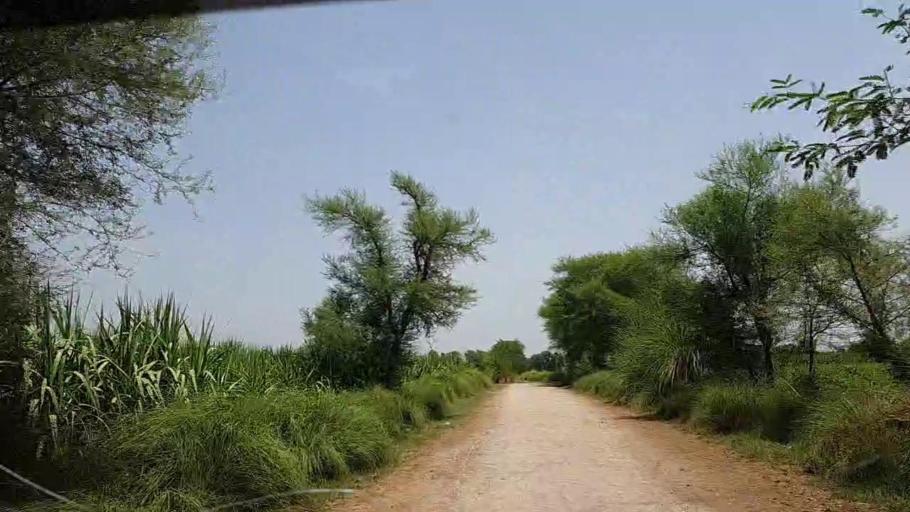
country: PK
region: Sindh
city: Tharu Shah
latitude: 26.9354
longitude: 68.0246
